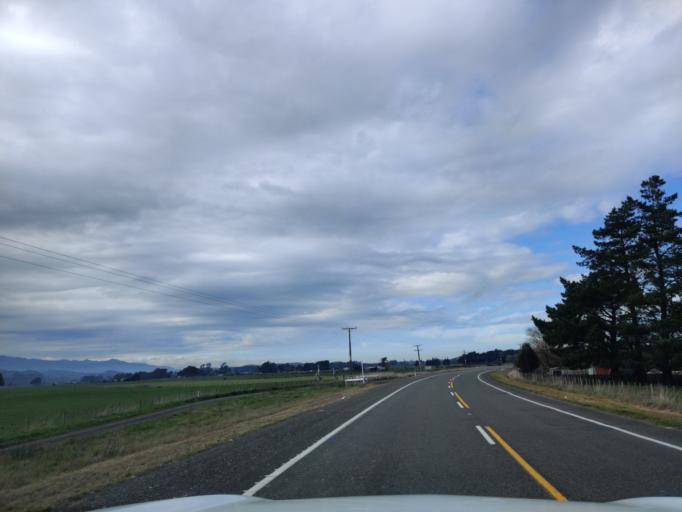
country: NZ
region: Manawatu-Wanganui
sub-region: Palmerston North City
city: Palmerston North
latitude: -40.3340
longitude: 175.8444
